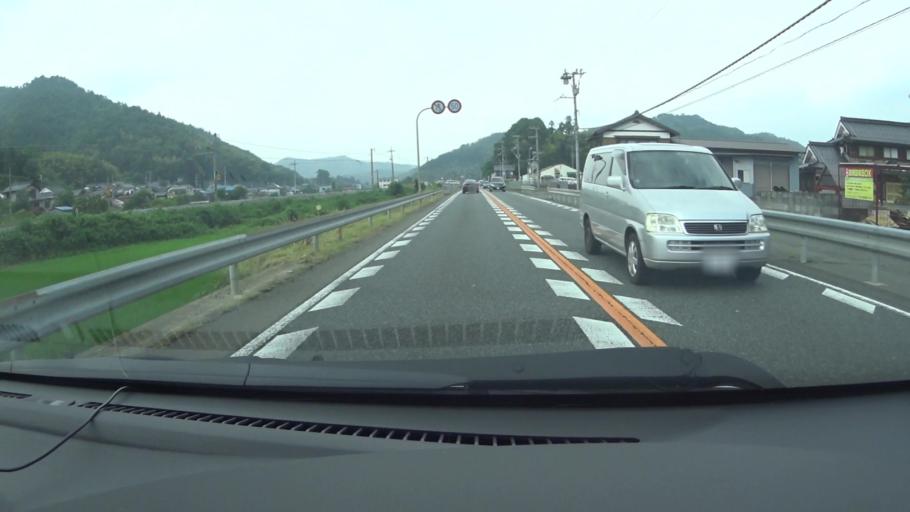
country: JP
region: Kyoto
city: Ayabe
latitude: 35.3435
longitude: 135.3115
